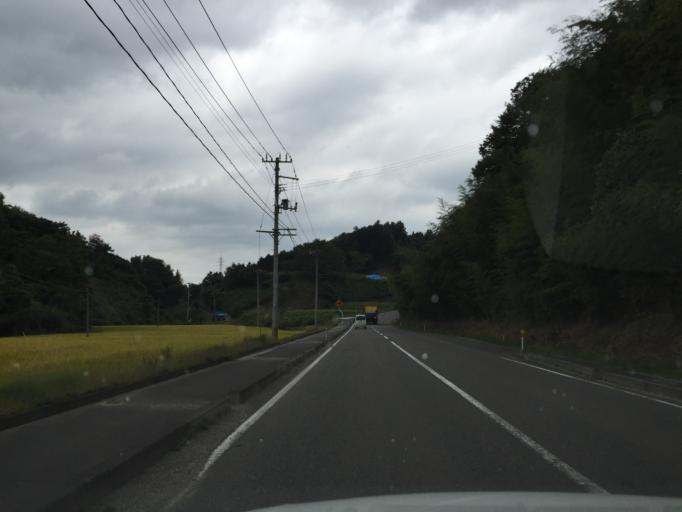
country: JP
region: Fukushima
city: Miharu
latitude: 37.4367
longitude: 140.5101
